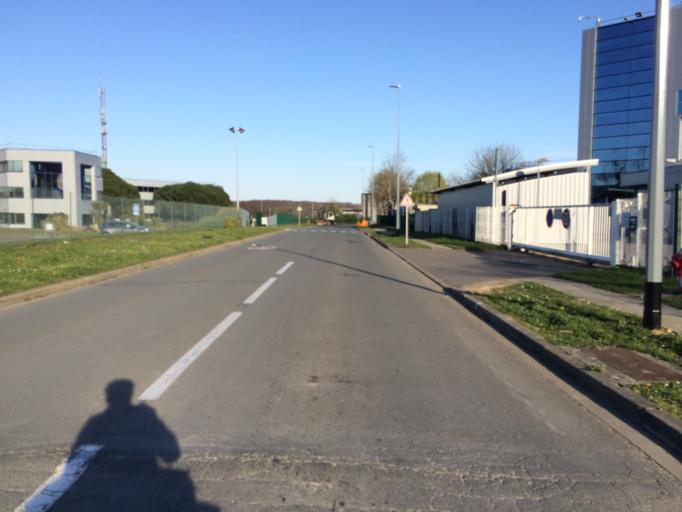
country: FR
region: Ile-de-France
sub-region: Departement de l'Essonne
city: Villejust
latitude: 48.6926
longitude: 2.2178
